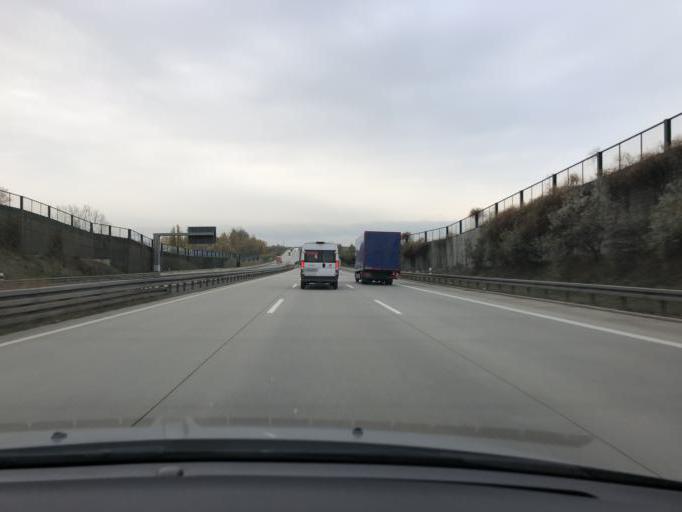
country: DE
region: Thuringia
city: Hermsdorf
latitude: 50.9004
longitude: 11.8432
